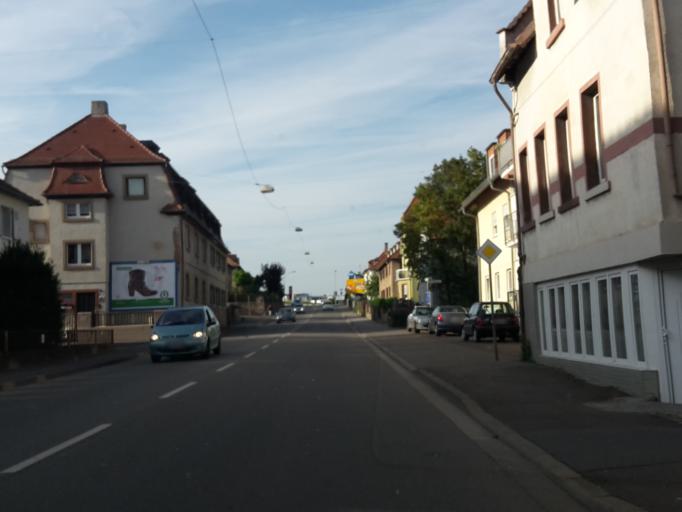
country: DE
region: Rheinland-Pfalz
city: Alzey
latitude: 49.7488
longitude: 8.1192
